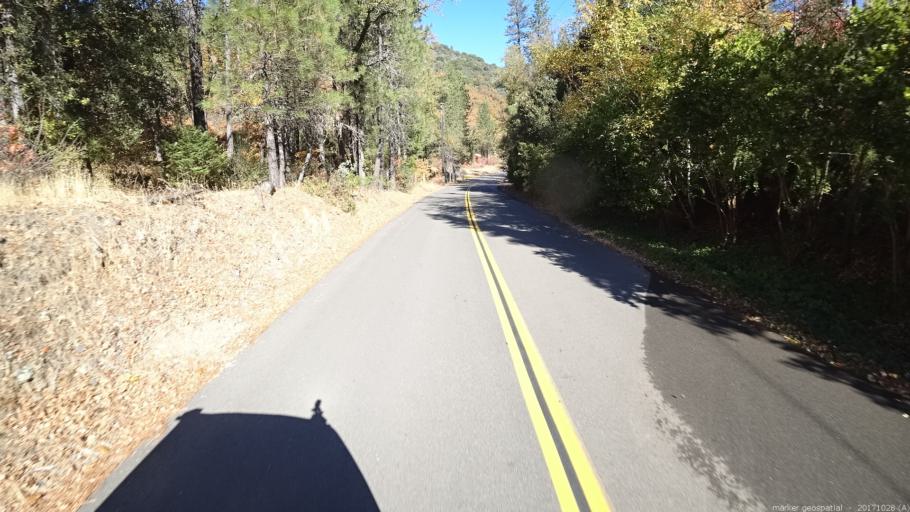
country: US
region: California
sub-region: Trinity County
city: Lewiston
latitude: 40.7607
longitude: -122.6150
